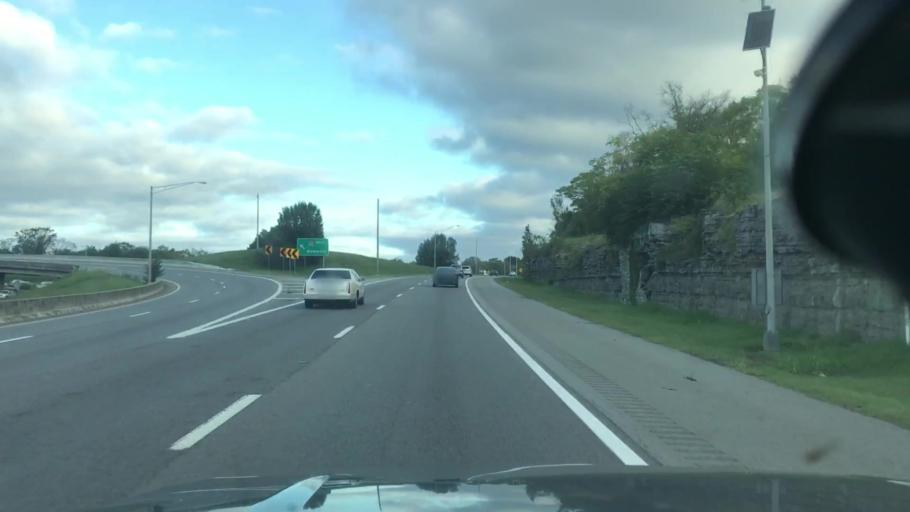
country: US
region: Tennessee
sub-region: Davidson County
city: Nashville
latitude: 36.1720
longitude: -86.7989
